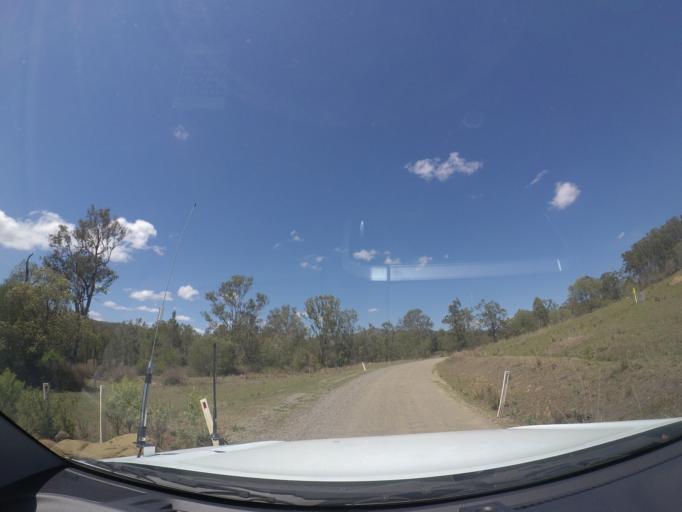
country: AU
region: Queensland
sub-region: Logan
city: Cedar Vale
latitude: -27.8625
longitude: 152.8544
